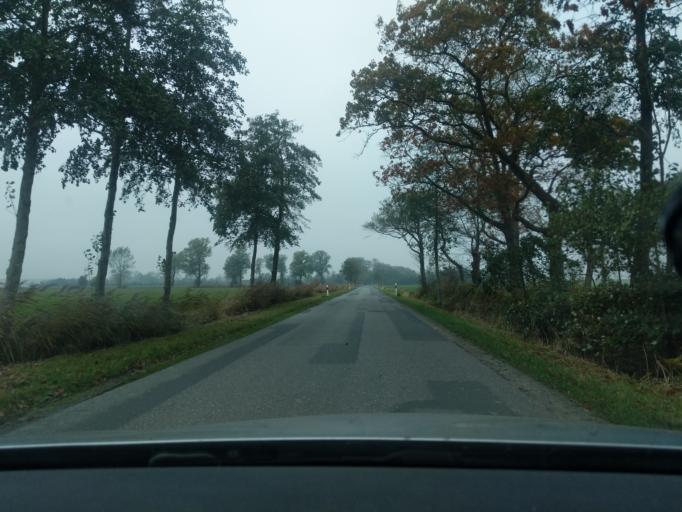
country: DE
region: Lower Saxony
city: Nordleda
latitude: 53.8262
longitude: 8.8208
